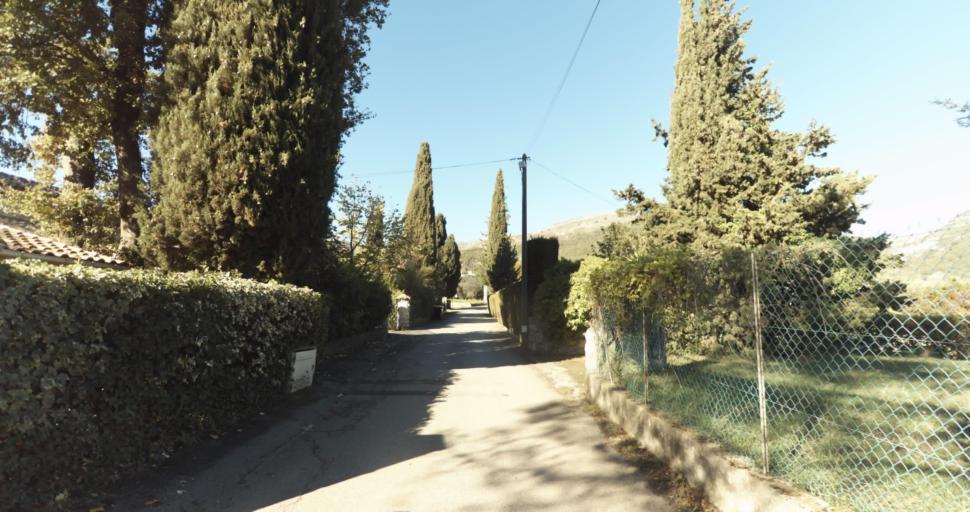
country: FR
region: Provence-Alpes-Cote d'Azur
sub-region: Departement des Alpes-Maritimes
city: Vence
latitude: 43.7204
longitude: 7.0908
